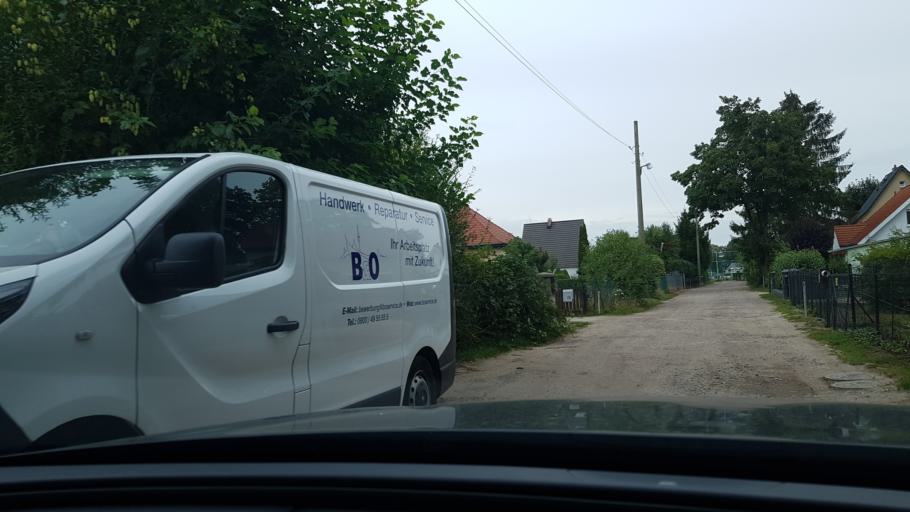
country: DE
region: Brandenburg
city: Brieselang
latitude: 52.5873
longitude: 12.9939
